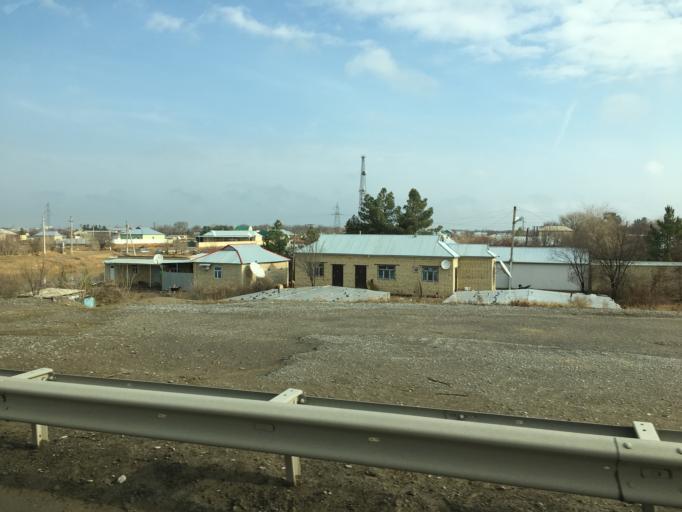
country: TM
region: Mary
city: Mary
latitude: 37.5505
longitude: 61.8634
